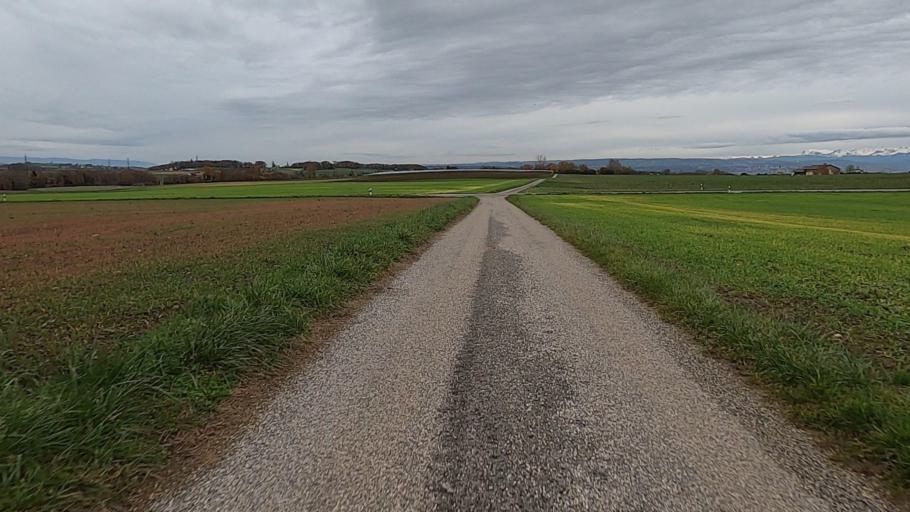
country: CH
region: Vaud
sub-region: Morges District
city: Apples
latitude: 46.5225
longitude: 6.4505
